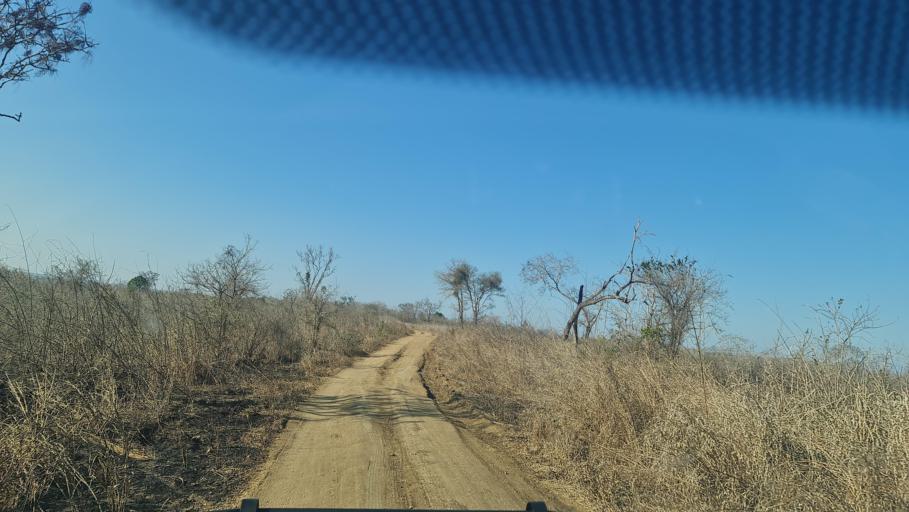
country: MZ
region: Nampula
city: Nacala
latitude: -13.9491
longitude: 40.4782
